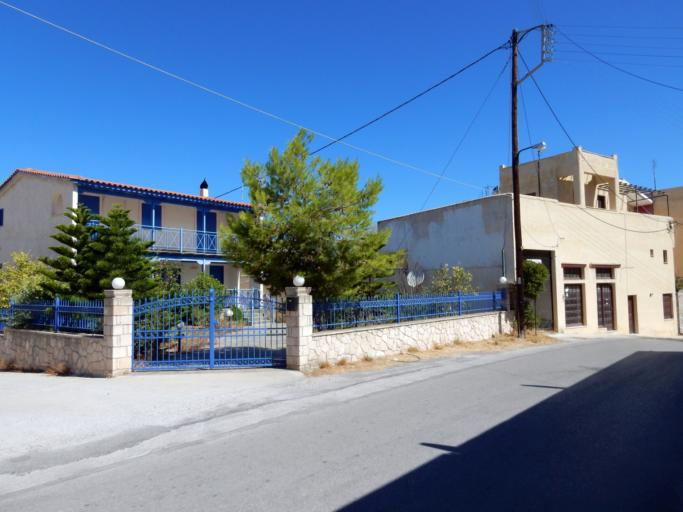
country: GR
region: Attica
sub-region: Nomos Piraios
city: Vathi
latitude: 37.7707
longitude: 23.4835
